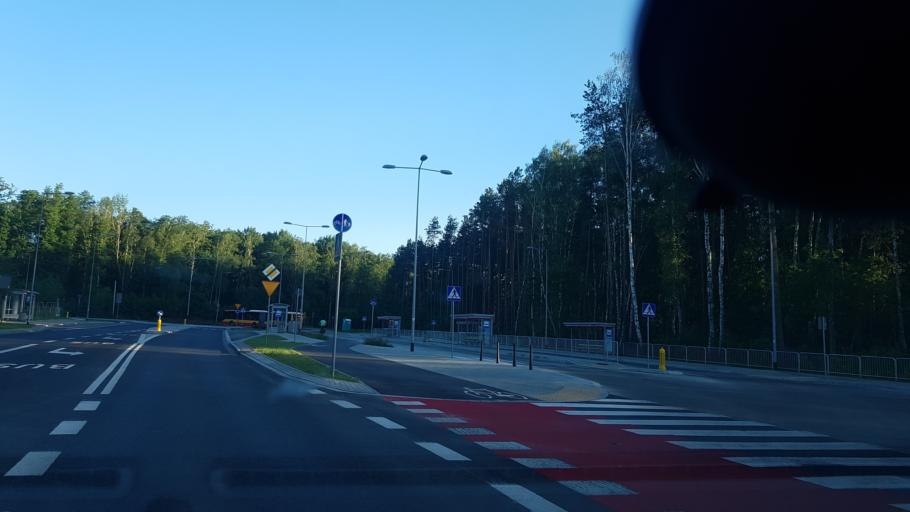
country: PL
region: Masovian Voivodeship
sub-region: Warszawa
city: Wesola
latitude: 52.2154
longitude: 21.2180
